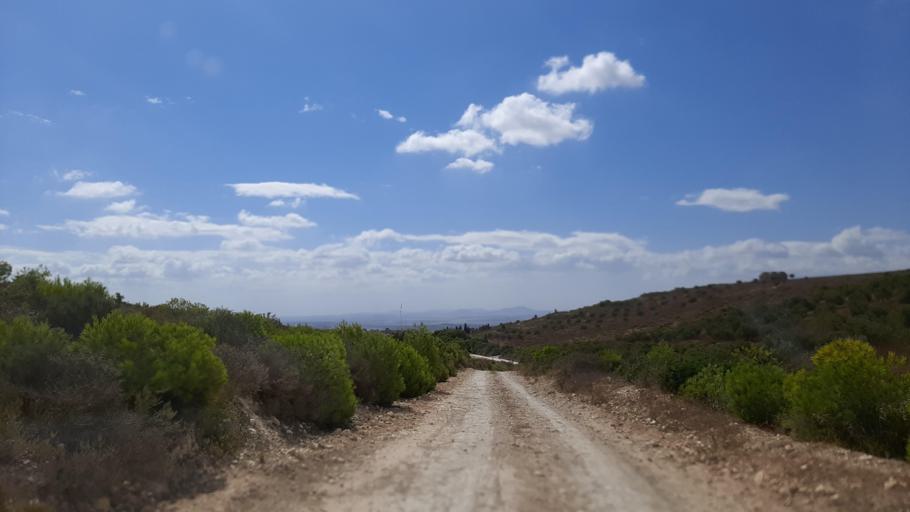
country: TN
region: Zaghwan
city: Zaghouan
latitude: 36.4957
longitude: 10.1738
